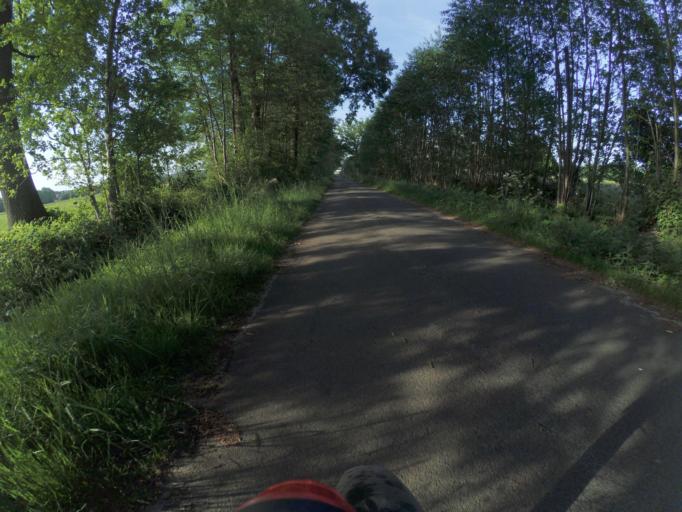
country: DE
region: North Rhine-Westphalia
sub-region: Regierungsbezirk Munster
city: Birgte
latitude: 52.2751
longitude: 7.6545
